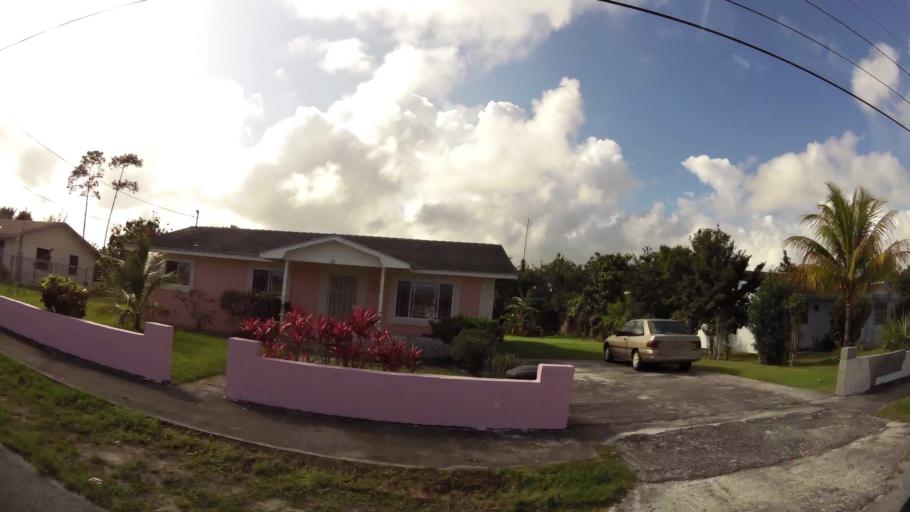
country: BS
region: Freeport
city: Lucaya
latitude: 26.5313
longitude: -78.6730
